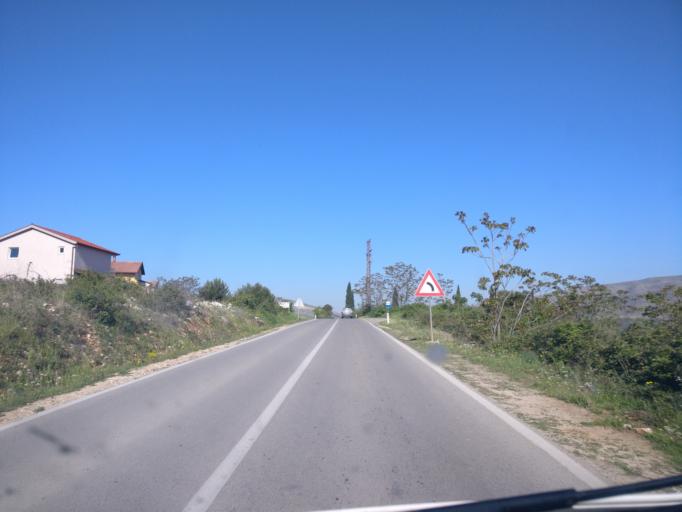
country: BA
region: Federation of Bosnia and Herzegovina
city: Tasovcici
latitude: 43.1192
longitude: 17.7356
